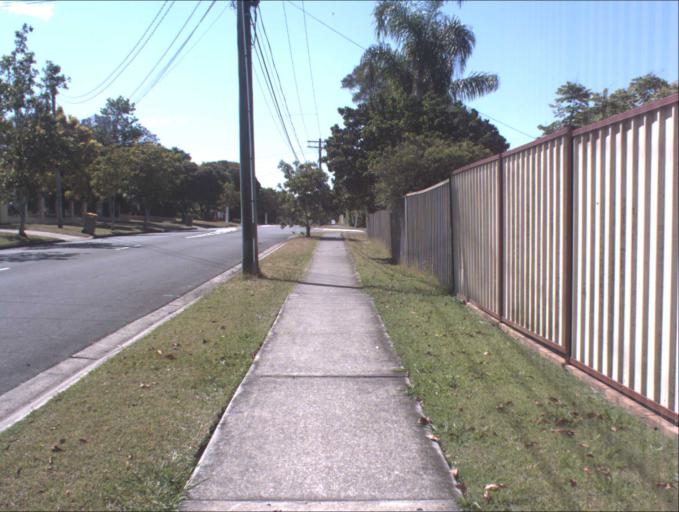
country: AU
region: Queensland
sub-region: Logan
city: Rochedale South
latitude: -27.5977
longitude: 153.1147
